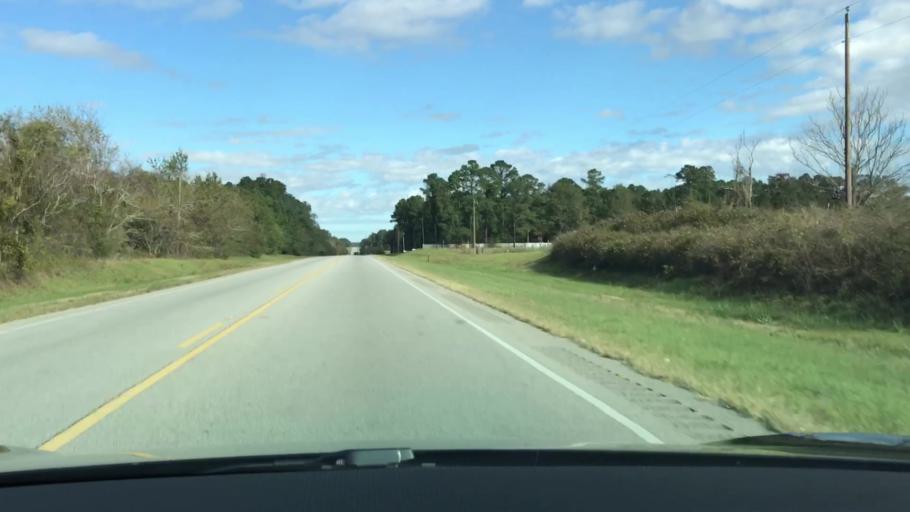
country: US
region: Georgia
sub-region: Jefferson County
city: Wadley
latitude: 32.9323
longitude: -82.3965
